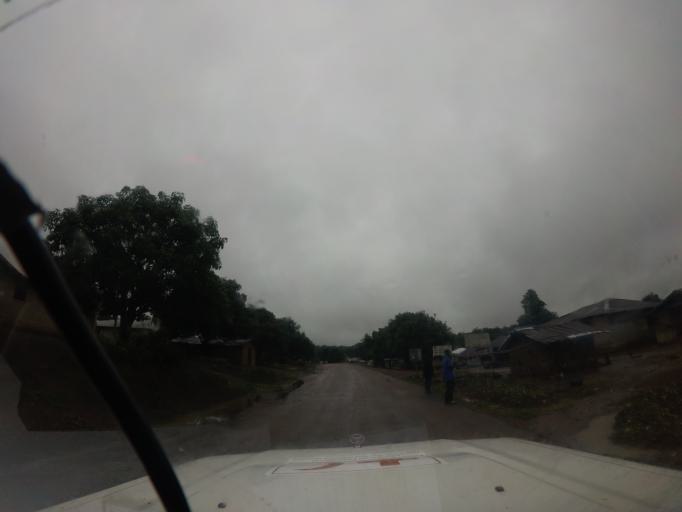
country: SL
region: Northern Province
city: Kabala
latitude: 9.5029
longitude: -11.5940
